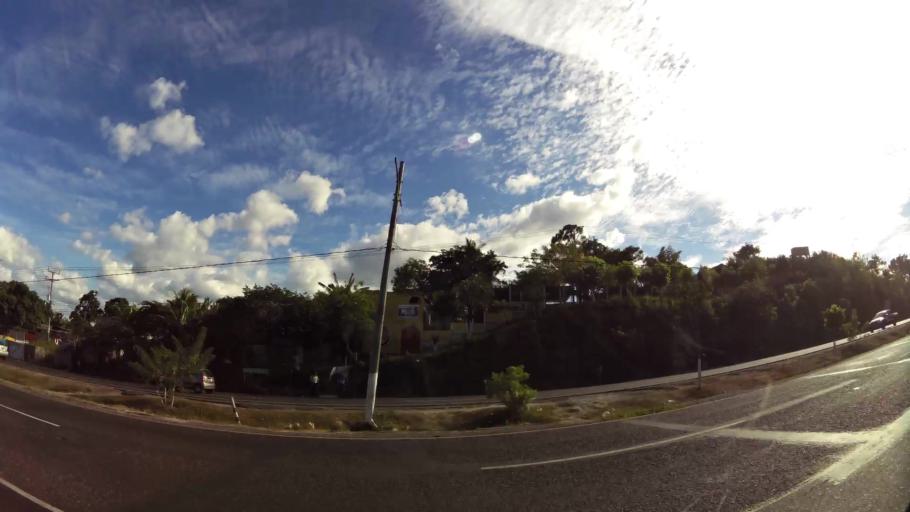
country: SV
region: San Salvador
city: Ilopango
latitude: 13.7341
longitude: -89.0634
